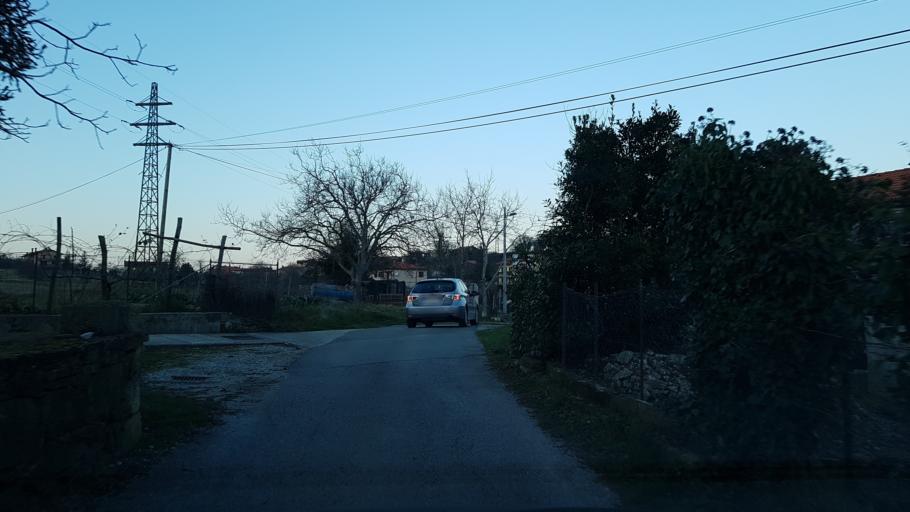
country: SI
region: Koper-Capodistria
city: Sv. Anton
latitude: 45.5211
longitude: 13.8681
